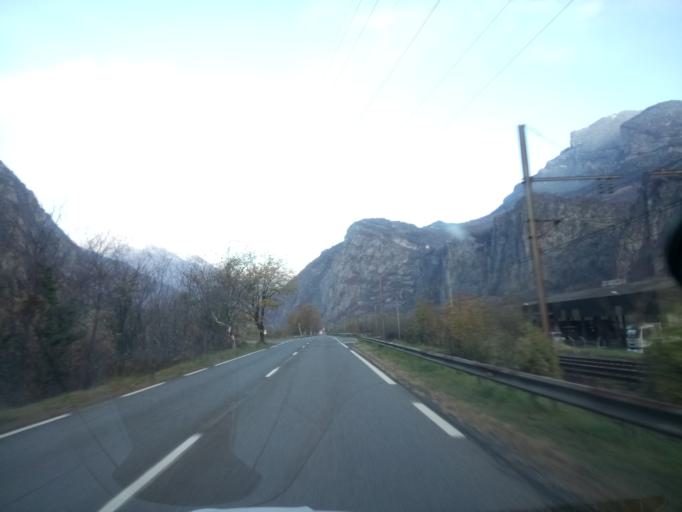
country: FR
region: Rhone-Alpes
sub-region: Departement de la Savoie
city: Saint-Jean-de-Maurienne
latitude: 45.3045
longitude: 6.3487
